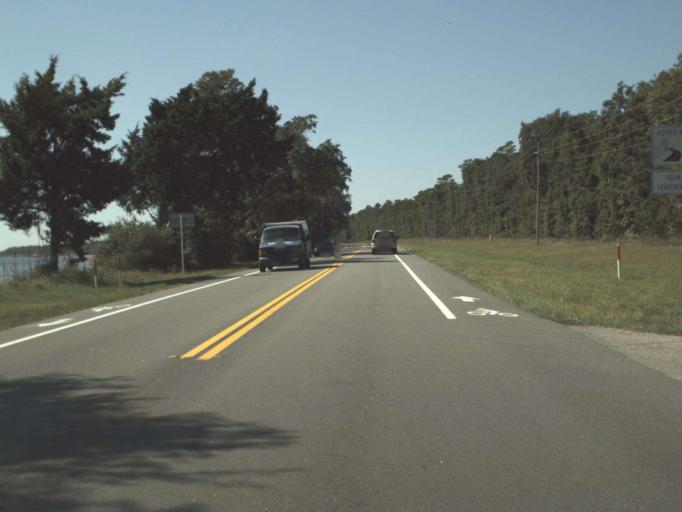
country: US
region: Florida
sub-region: Walton County
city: Miramar Beach
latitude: 30.4650
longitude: -86.3684
